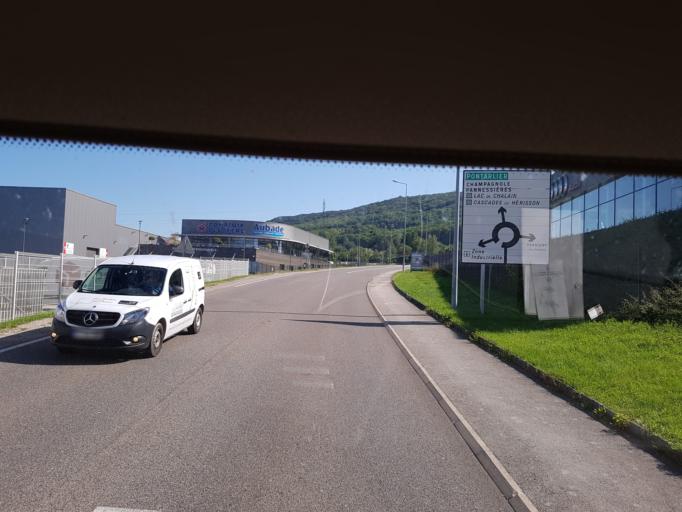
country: FR
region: Franche-Comte
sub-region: Departement du Jura
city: Perrigny
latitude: 46.6744
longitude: 5.5817
